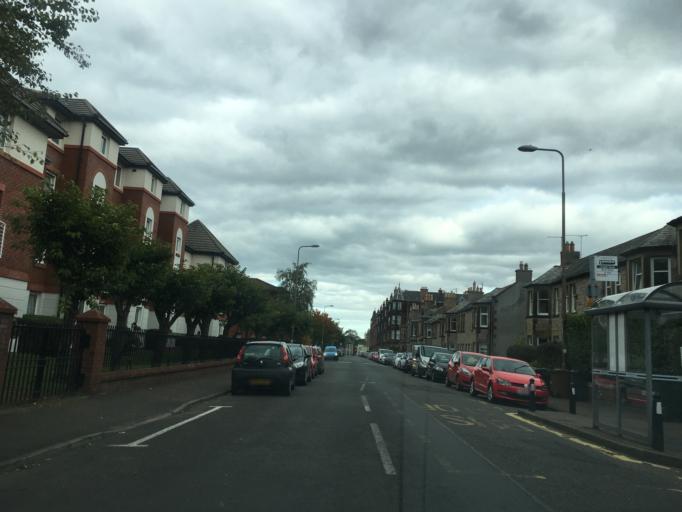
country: GB
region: Scotland
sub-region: Edinburgh
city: Edinburgh
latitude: 55.9284
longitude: -3.1798
